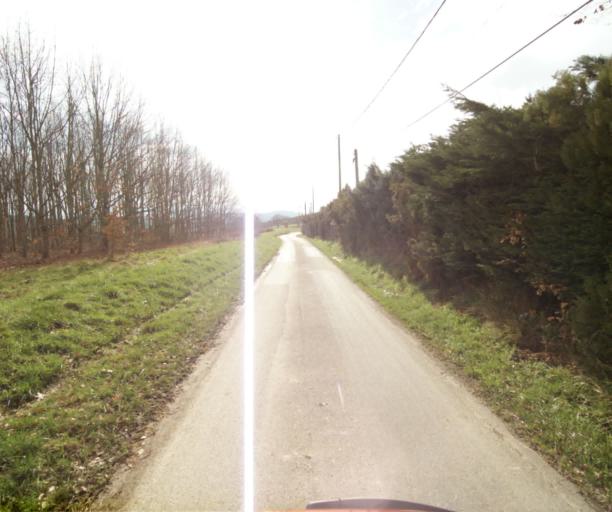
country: FR
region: Midi-Pyrenees
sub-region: Departement de l'Ariege
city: La Tour-du-Crieu
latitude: 43.0862
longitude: 1.7423
